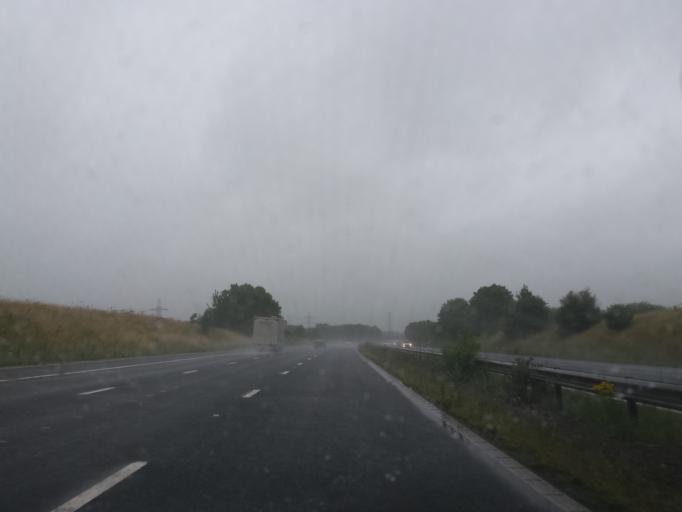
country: GB
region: England
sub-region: Leicestershire
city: Croft
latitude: 52.5719
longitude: -1.2650
